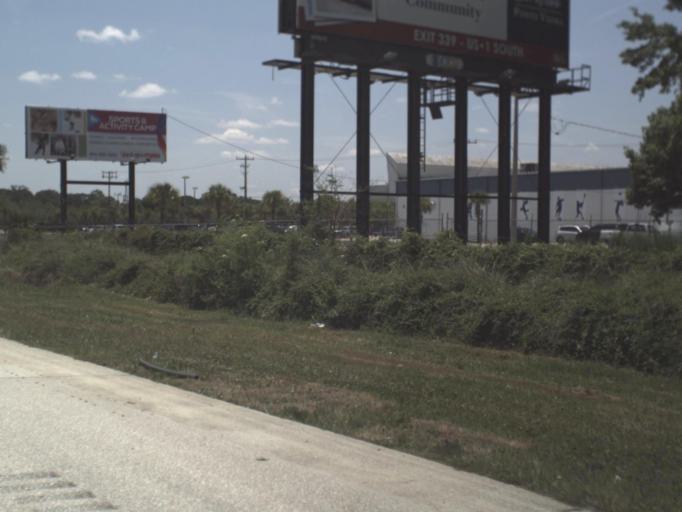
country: US
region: Florida
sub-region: Duval County
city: Jacksonville
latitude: 30.2933
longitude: -81.6328
